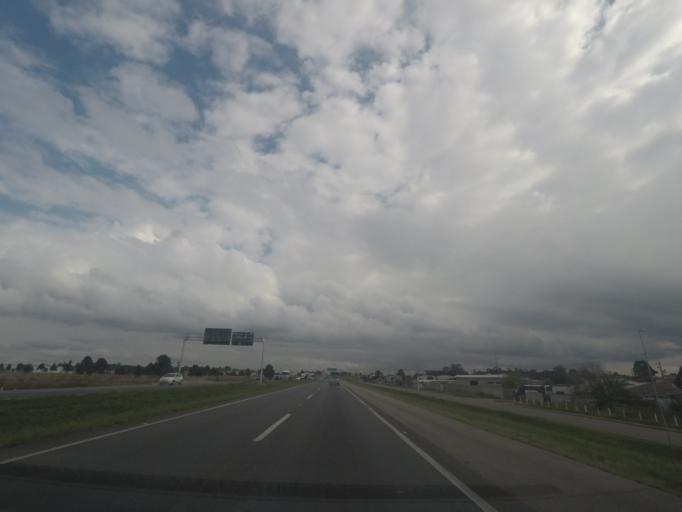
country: BR
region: Parana
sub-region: Piraquara
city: Piraquara
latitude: -25.5041
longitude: -49.1227
